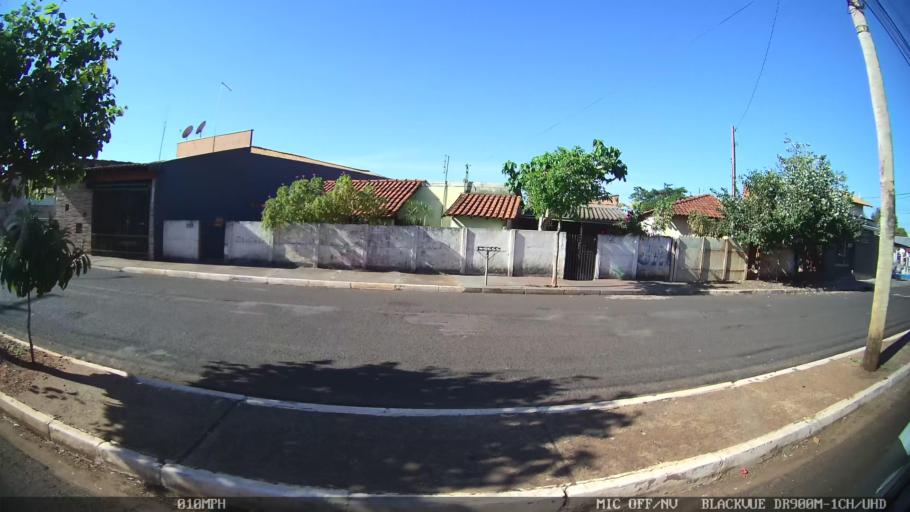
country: BR
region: Sao Paulo
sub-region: Olimpia
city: Olimpia
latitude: -20.7521
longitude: -48.9076
